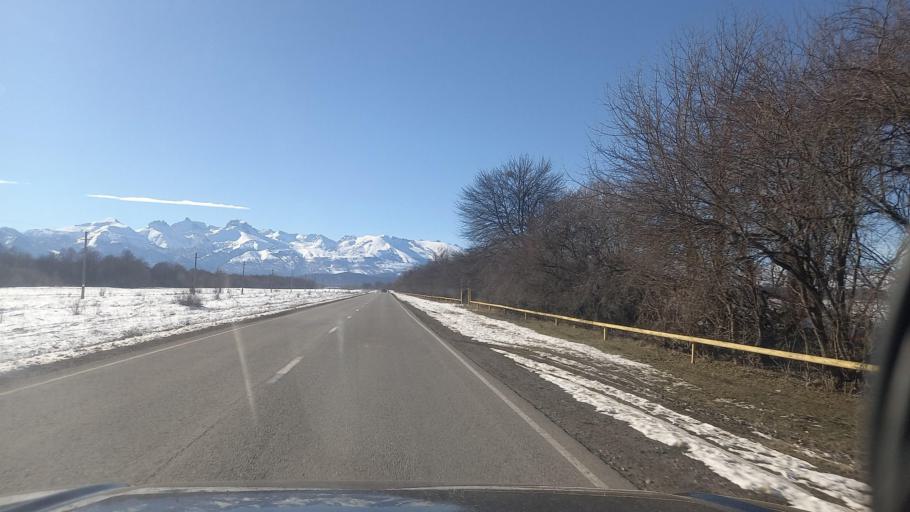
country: RU
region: North Ossetia
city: Chikola
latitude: 43.1782
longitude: 43.8830
